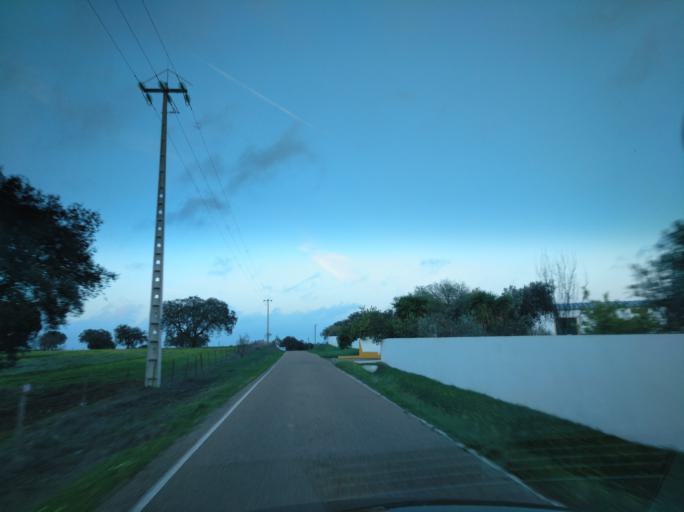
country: PT
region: Portalegre
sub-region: Campo Maior
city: Campo Maior
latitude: 39.0696
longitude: -7.1167
